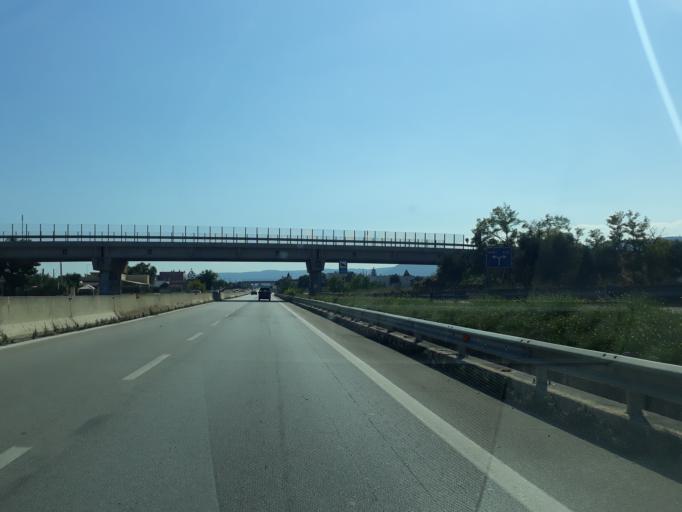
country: IT
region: Apulia
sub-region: Provincia di Brindisi
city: Fasano
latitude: 40.8736
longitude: 17.3416
